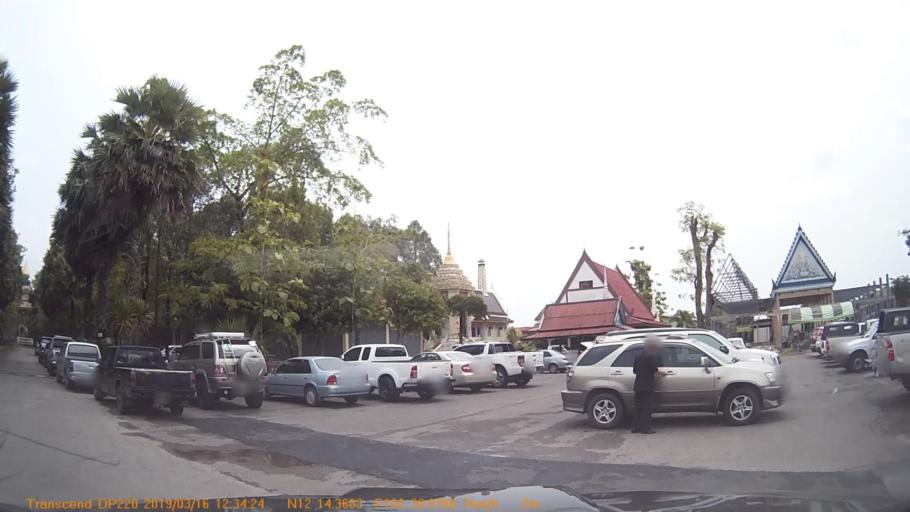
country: TH
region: Trat
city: Trat
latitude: 12.2394
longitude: 102.5163
